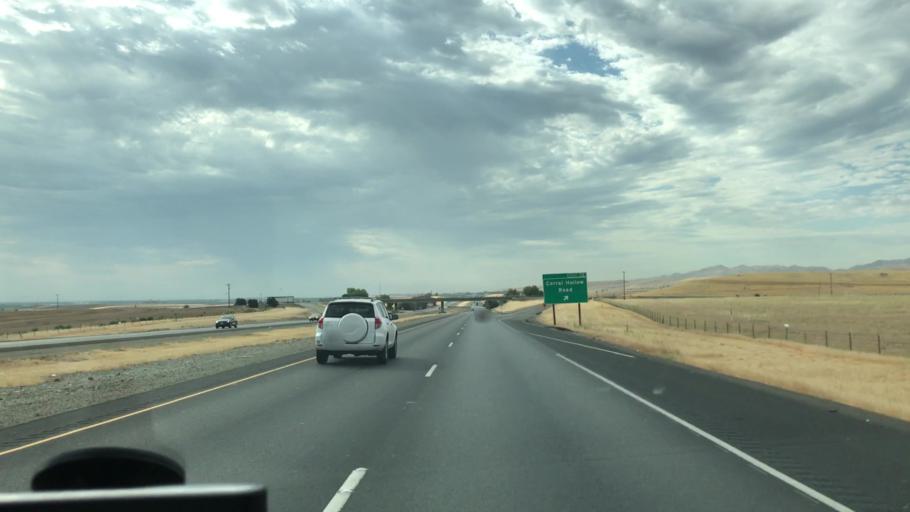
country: US
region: California
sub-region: San Joaquin County
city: Tracy
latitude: 37.6745
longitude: -121.4614
